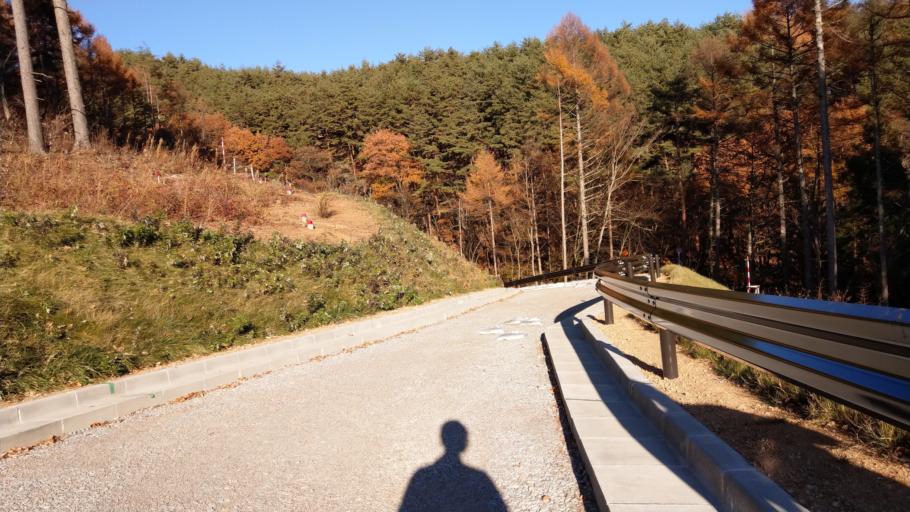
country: JP
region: Nagano
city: Komoro
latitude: 36.3634
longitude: 138.4316
